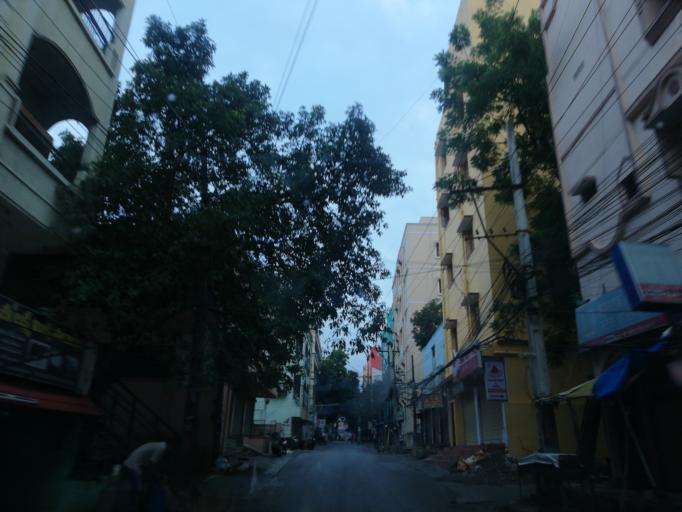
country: IN
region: Telangana
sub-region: Rangareddi
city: Kukatpalli
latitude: 17.4907
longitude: 78.3978
